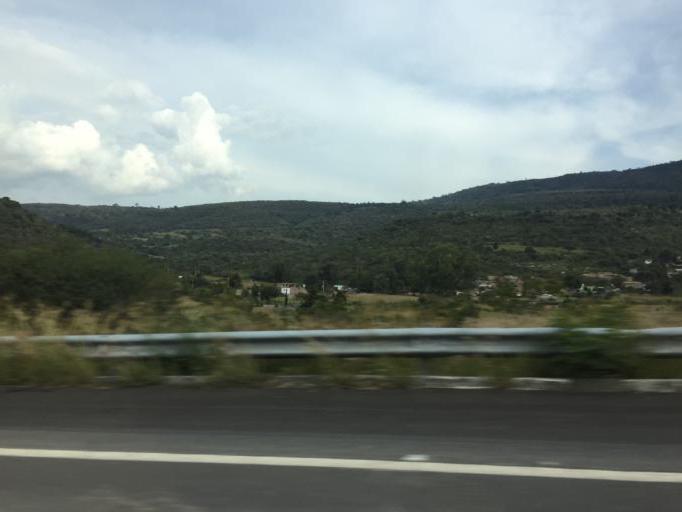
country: MX
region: Mexico
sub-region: Chapultepec
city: Chucandiro
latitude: 19.8913
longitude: -101.3090
